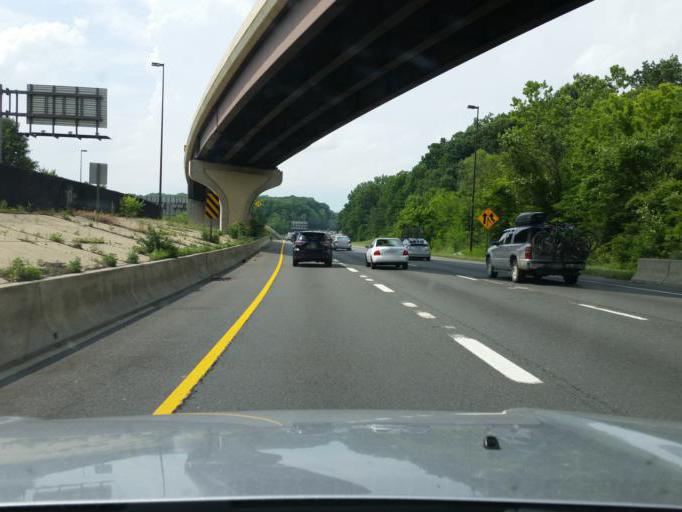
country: US
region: Maryland
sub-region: Montgomery County
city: North Bethesda
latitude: 39.0339
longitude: -77.1427
